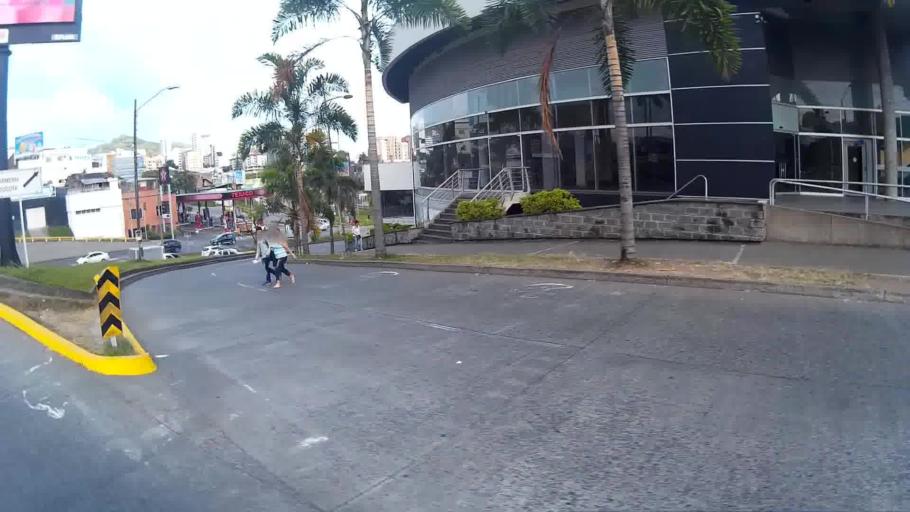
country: CO
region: Risaralda
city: Pereira
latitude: 4.8080
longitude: -75.6939
